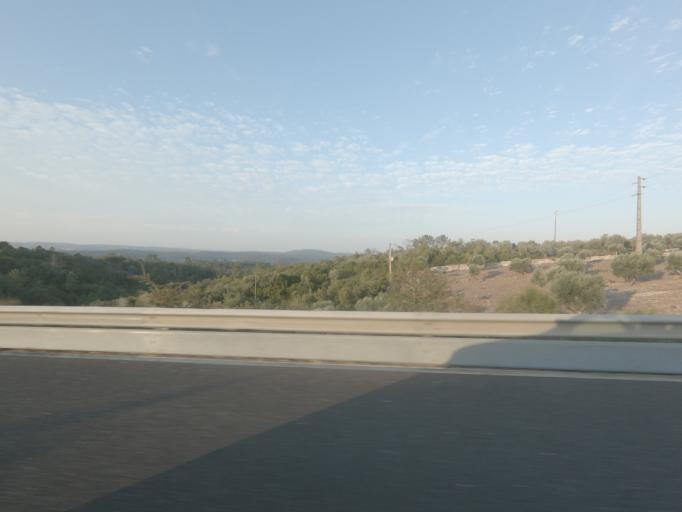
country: PT
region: Leiria
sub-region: Leiria
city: Santa Catarina da Serra
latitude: 39.6912
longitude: -8.6908
